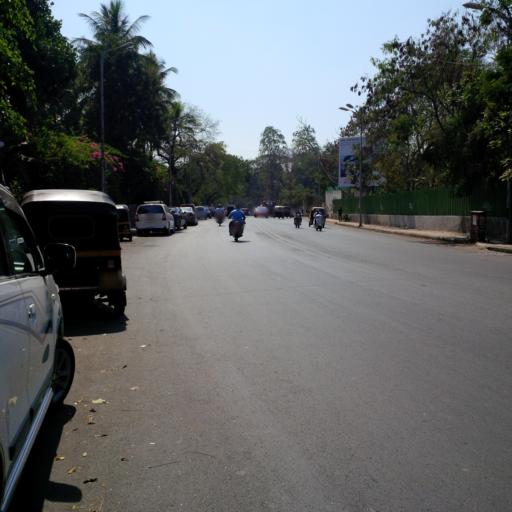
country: IN
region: Maharashtra
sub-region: Pune Division
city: Shivaji Nagar
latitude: 18.5189
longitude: 73.8304
